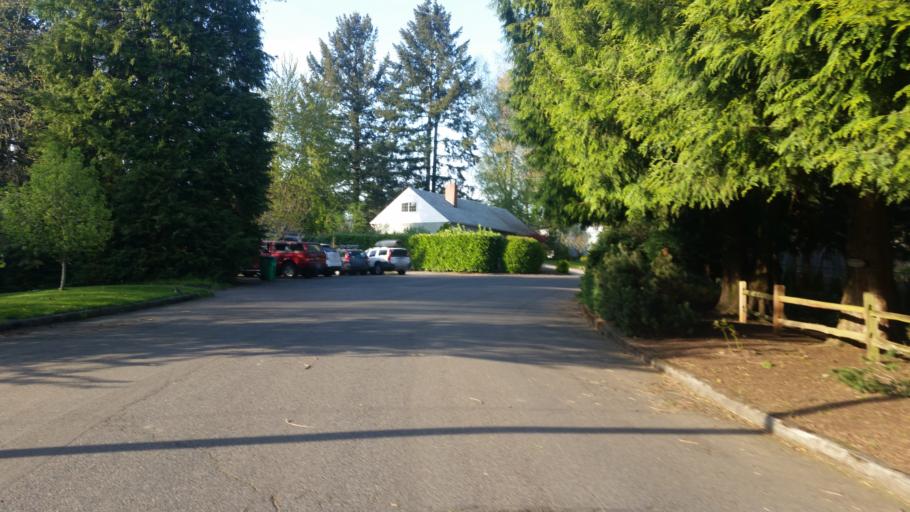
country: US
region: Oregon
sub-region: Washington County
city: Garden Home-Whitford
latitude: 45.4779
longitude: -122.7272
